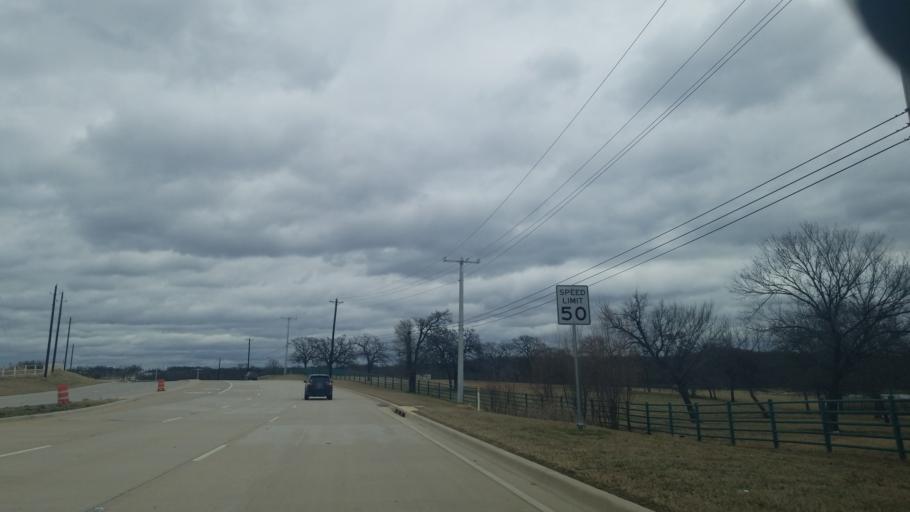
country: US
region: Texas
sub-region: Denton County
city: Bartonville
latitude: 33.0475
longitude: -97.1401
